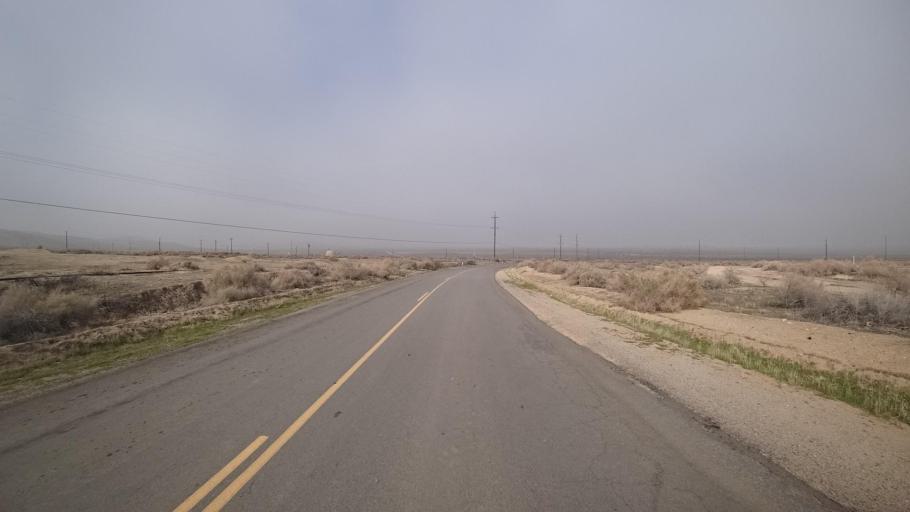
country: US
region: California
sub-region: Kern County
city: Ford City
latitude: 35.1781
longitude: -119.4286
